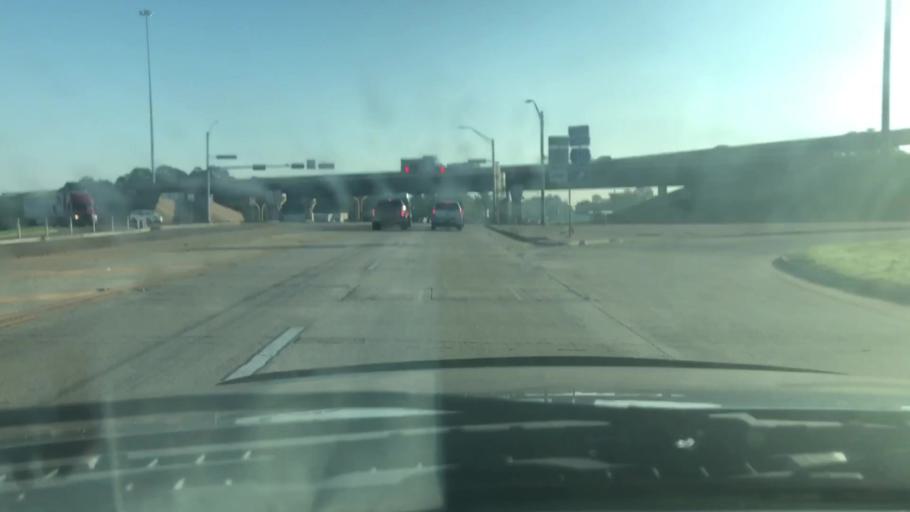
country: US
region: Texas
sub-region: Bowie County
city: Wake Village
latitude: 33.3940
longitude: -94.0994
